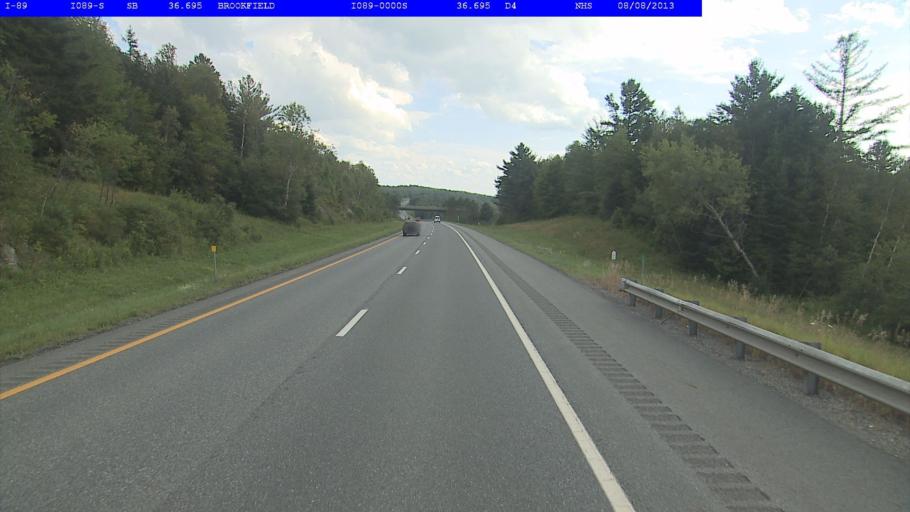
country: US
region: Vermont
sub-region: Orange County
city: Randolph
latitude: 44.0283
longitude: -72.6175
